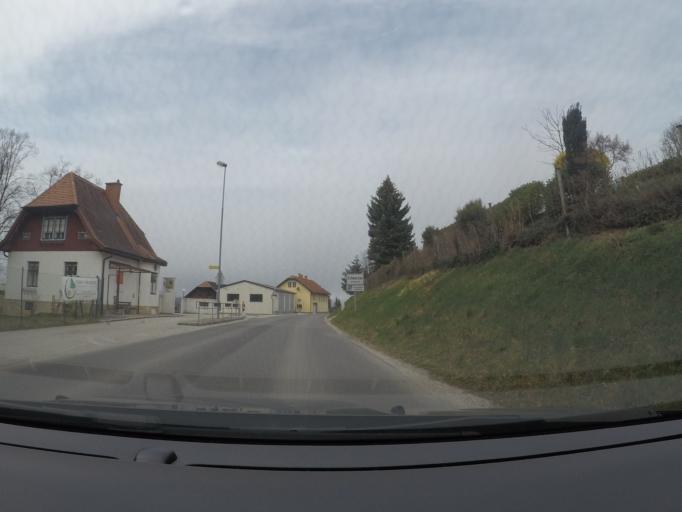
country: AT
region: Lower Austria
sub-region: Politischer Bezirk Neunkirchen
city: Pitten
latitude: 47.7238
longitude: 16.1798
